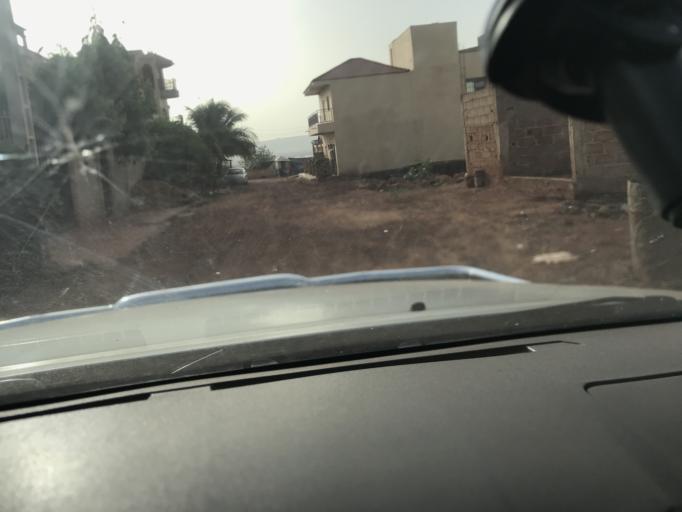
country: ML
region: Bamako
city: Bamako
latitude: 12.5890
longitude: -8.0074
